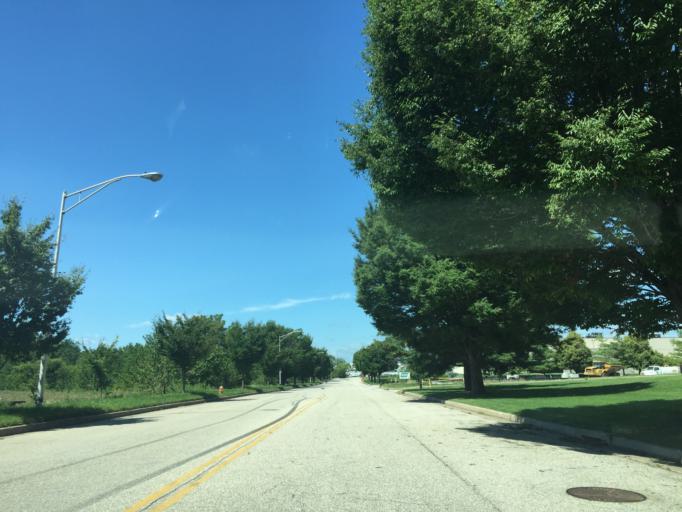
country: US
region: Maryland
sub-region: Baltimore County
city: Dundalk
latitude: 39.2676
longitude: -76.5360
